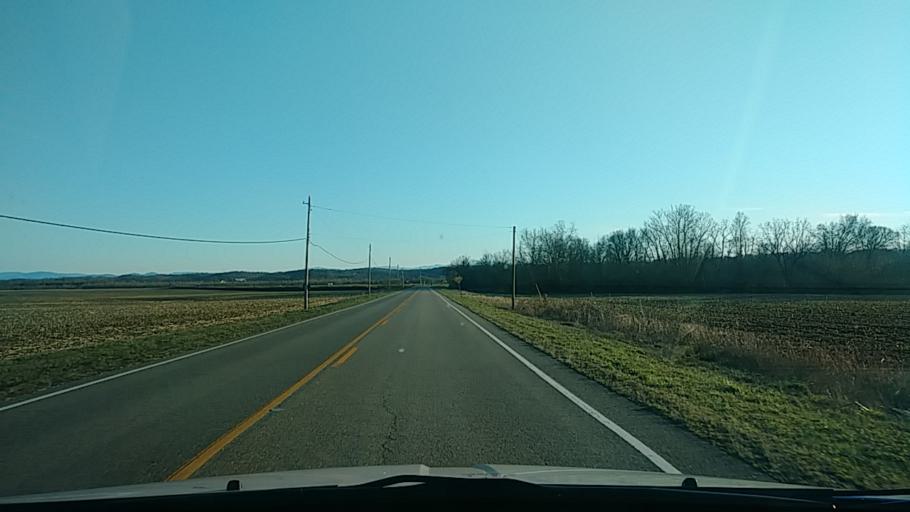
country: US
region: Tennessee
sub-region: Hamblen County
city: Morristown
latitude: 36.1716
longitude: -83.1602
